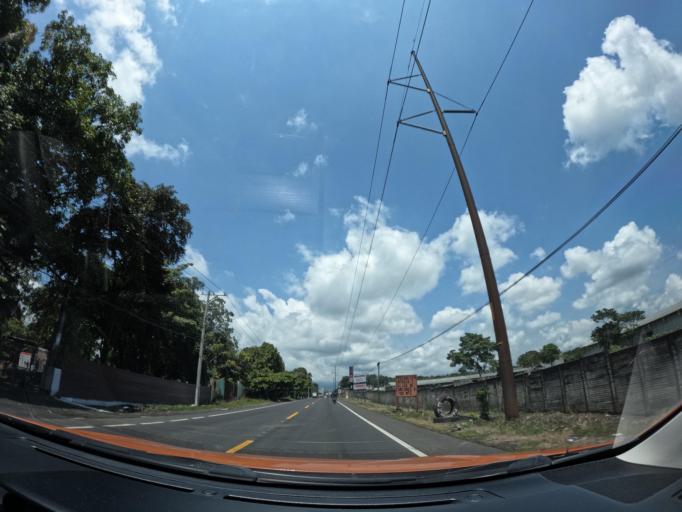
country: GT
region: Escuintla
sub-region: Municipio de Escuintla
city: Escuintla
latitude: 14.2724
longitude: -90.7918
